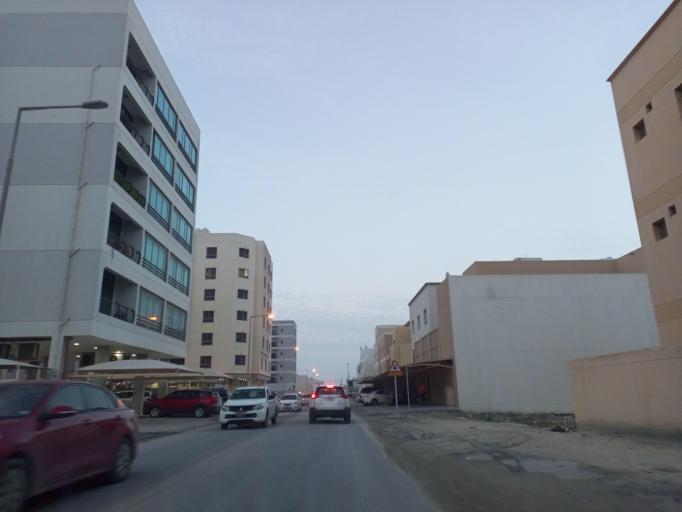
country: BH
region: Muharraq
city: Al Hadd
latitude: 26.2320
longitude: 50.6481
